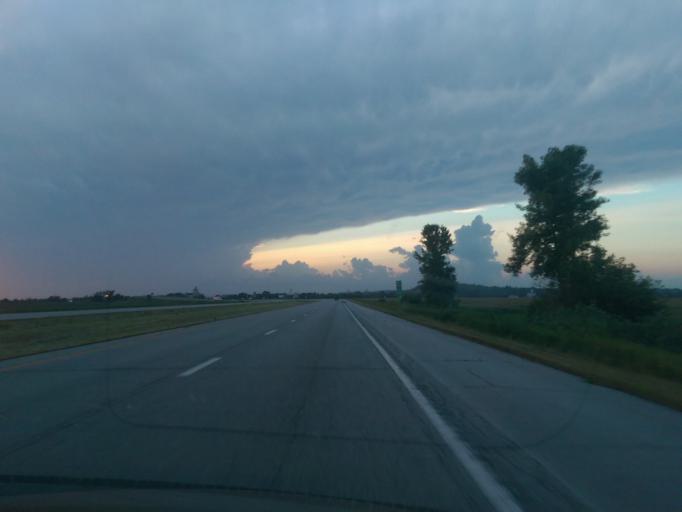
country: US
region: Iowa
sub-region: Fremont County
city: Hamburg
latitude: 40.5800
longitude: -95.6485
